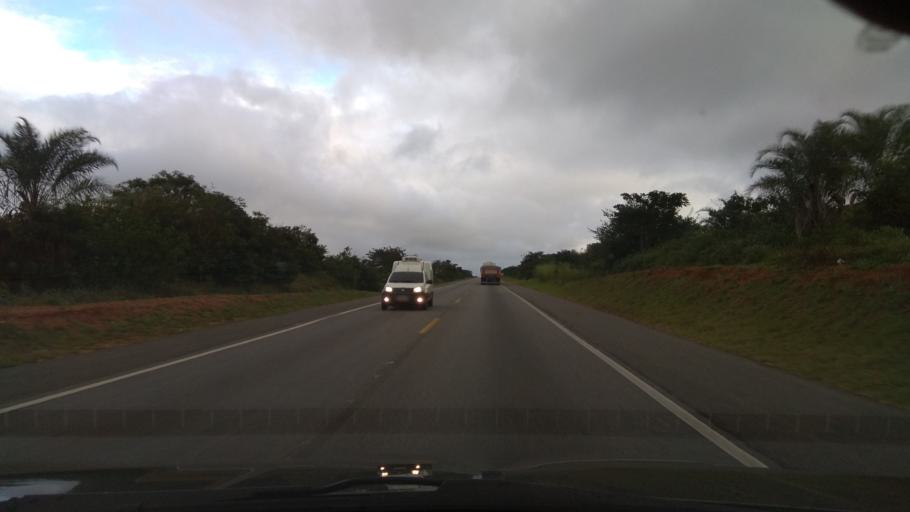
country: BR
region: Bahia
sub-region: Jaguaquara
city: Jaguaquara
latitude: -13.3421
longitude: -40.0166
